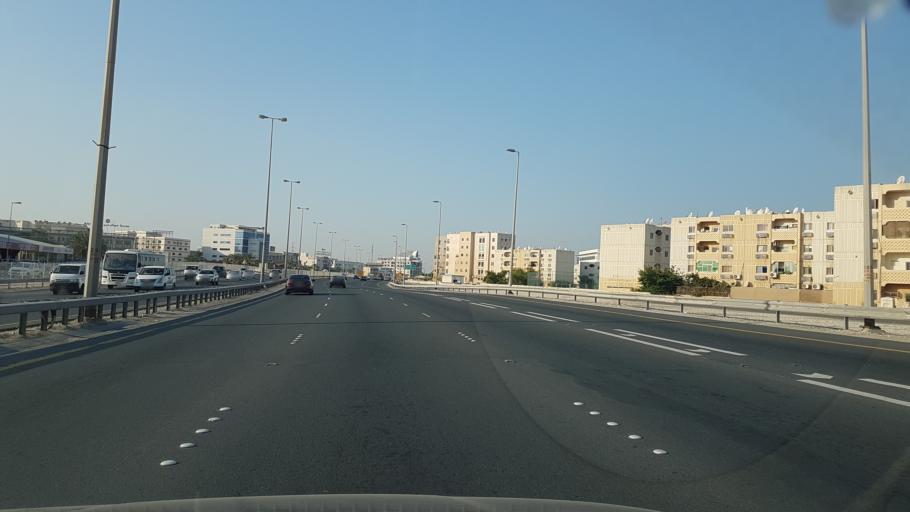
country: BH
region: Northern
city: Madinat `Isa
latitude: 26.1781
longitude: 50.5396
